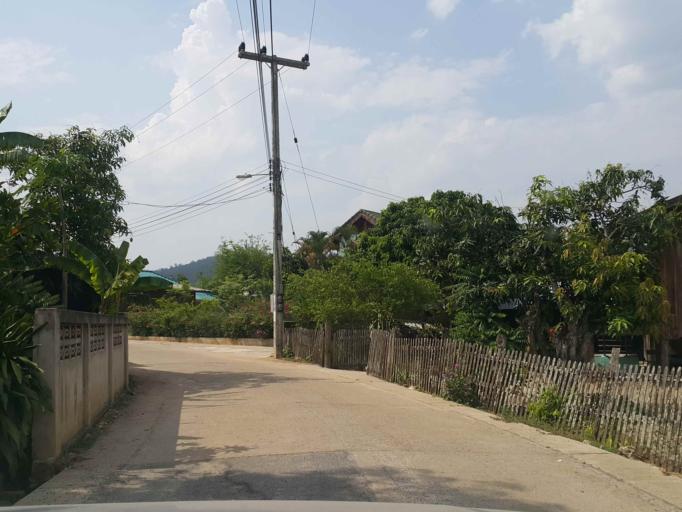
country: TH
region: Chiang Mai
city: Wiang Haeng
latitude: 19.3856
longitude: 98.7166
